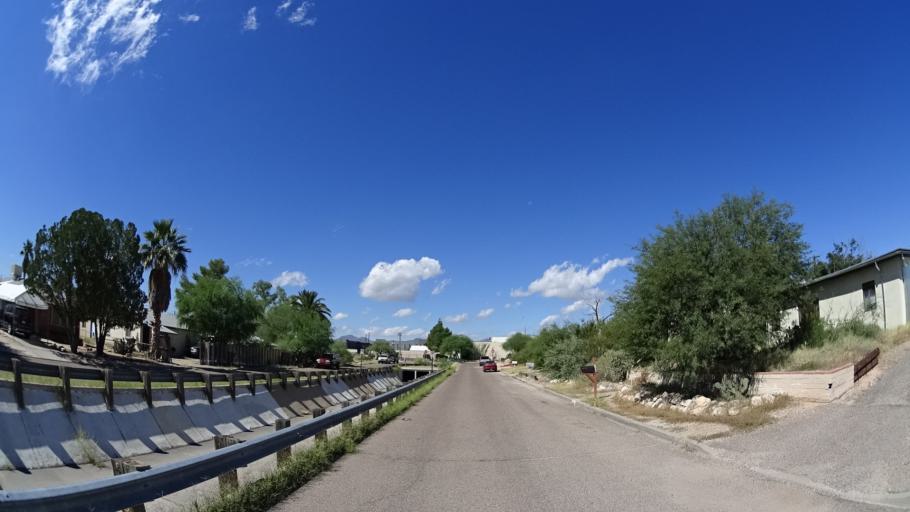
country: US
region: Arizona
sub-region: Pima County
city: South Tucson
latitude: 32.2448
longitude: -110.9677
